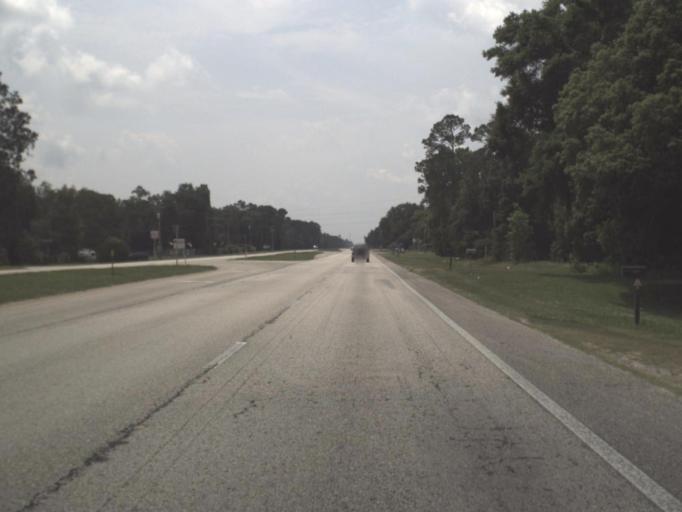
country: US
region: Florida
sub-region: Clay County
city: Green Cove Springs
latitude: 29.9296
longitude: -81.6870
